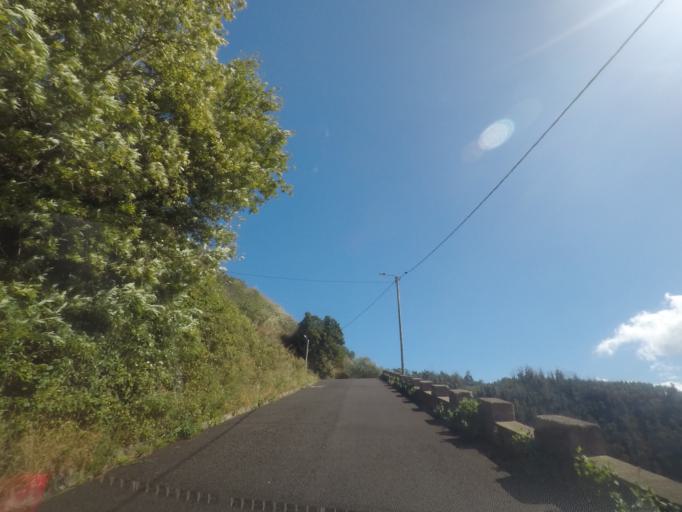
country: PT
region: Madeira
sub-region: Ribeira Brava
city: Campanario
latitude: 32.6924
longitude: -17.0390
